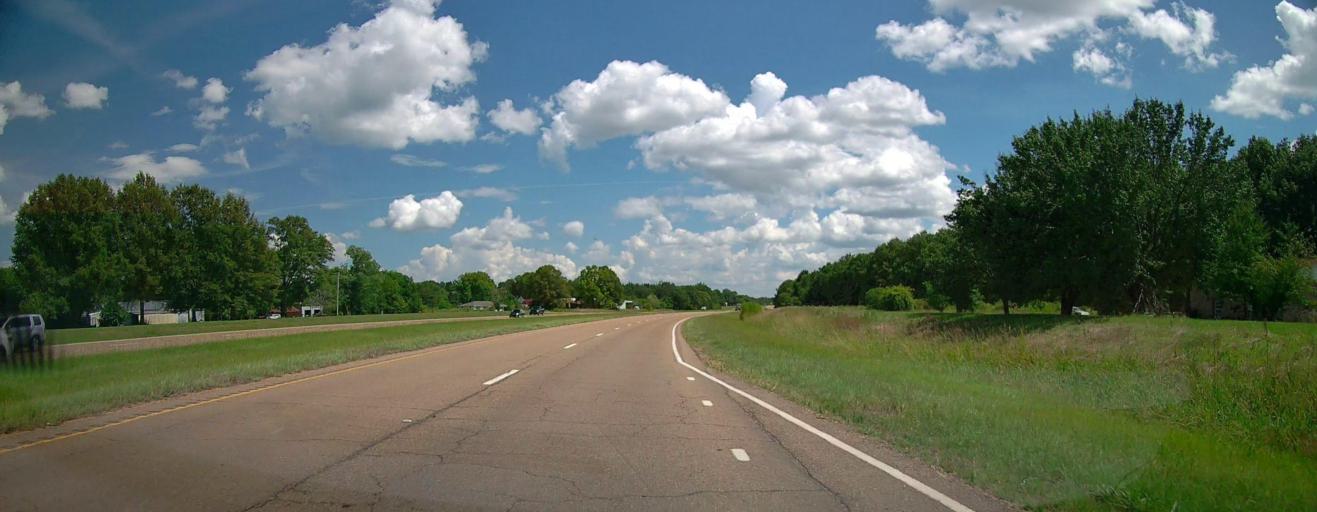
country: US
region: Mississippi
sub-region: Monroe County
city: Aberdeen
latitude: 33.8032
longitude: -88.4662
